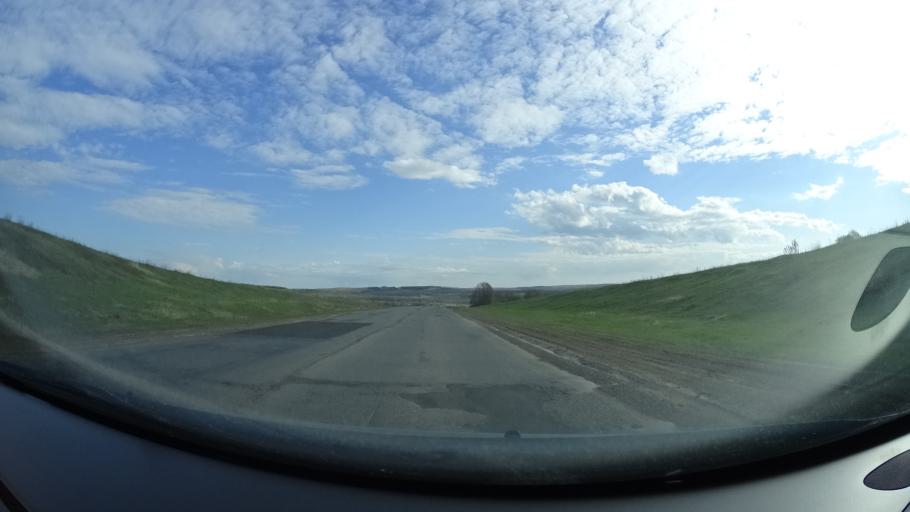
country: RU
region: Bashkortostan
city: Blagoveshchensk
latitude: 55.0977
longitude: 55.8183
